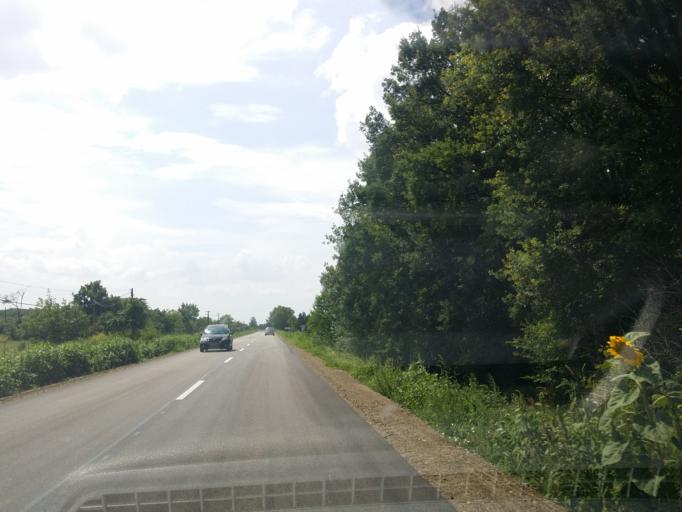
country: HU
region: Heves
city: Poroszlo
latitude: 47.6271
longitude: 20.6070
